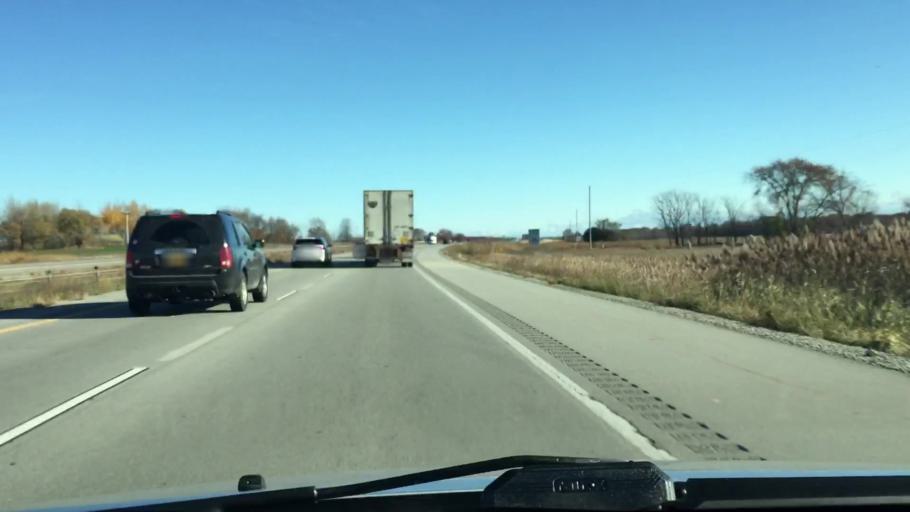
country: US
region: Wisconsin
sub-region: Brown County
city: De Pere
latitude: 44.4191
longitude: -88.1298
